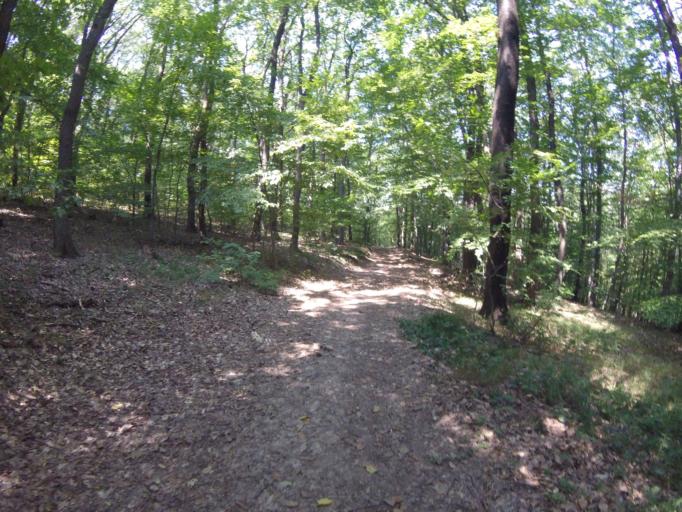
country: HU
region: Baranya
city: Pellerd
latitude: 46.0960
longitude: 18.1651
